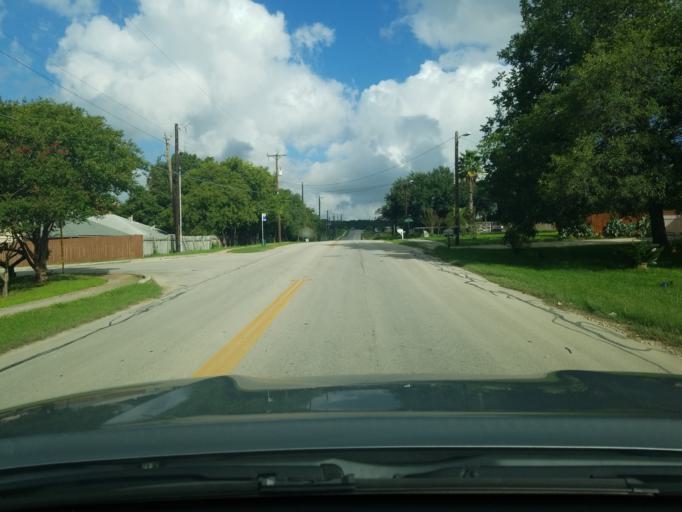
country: US
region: Texas
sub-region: Bexar County
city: Live Oak
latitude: 29.5785
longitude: -98.3622
